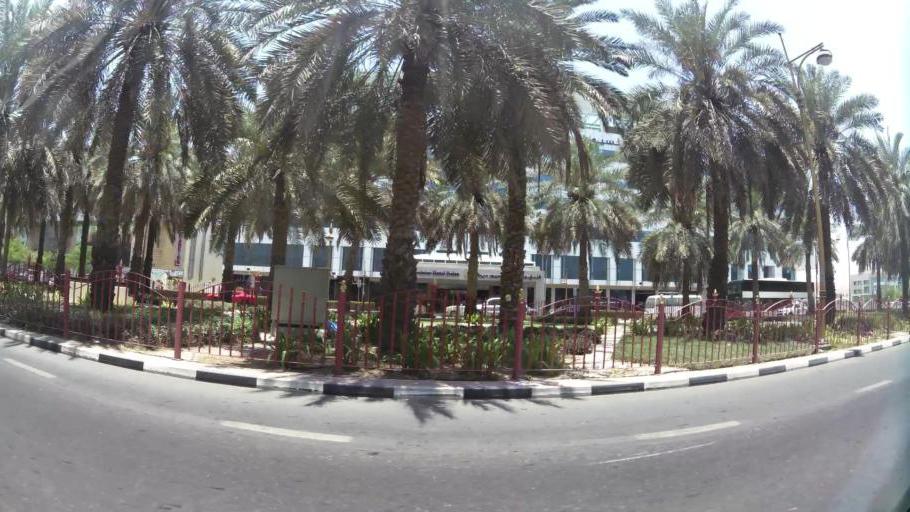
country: AE
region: Ash Shariqah
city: Sharjah
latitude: 25.2744
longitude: 55.3275
